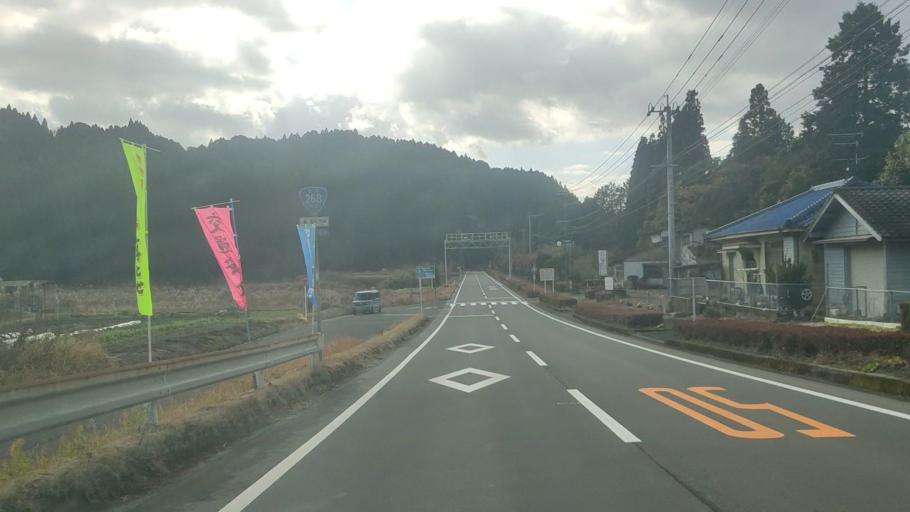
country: JP
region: Kagoshima
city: Okuchi-shinohara
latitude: 31.9638
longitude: 130.7380
